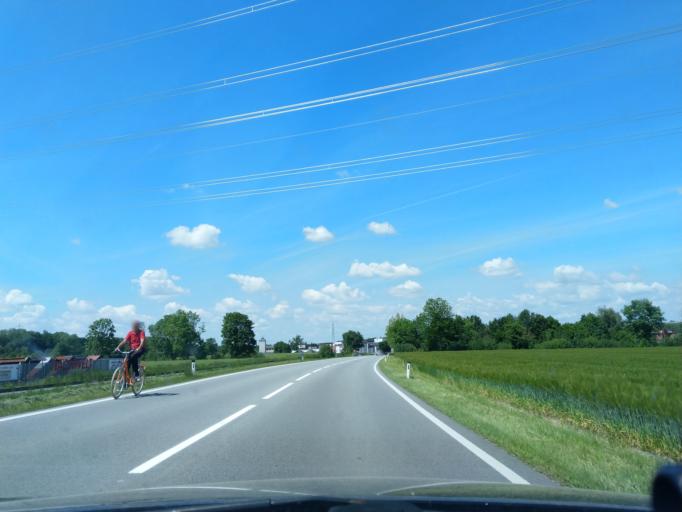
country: AT
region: Upper Austria
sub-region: Politischer Bezirk Ried im Innkreis
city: Ried im Innkreis
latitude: 48.2214
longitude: 13.4779
